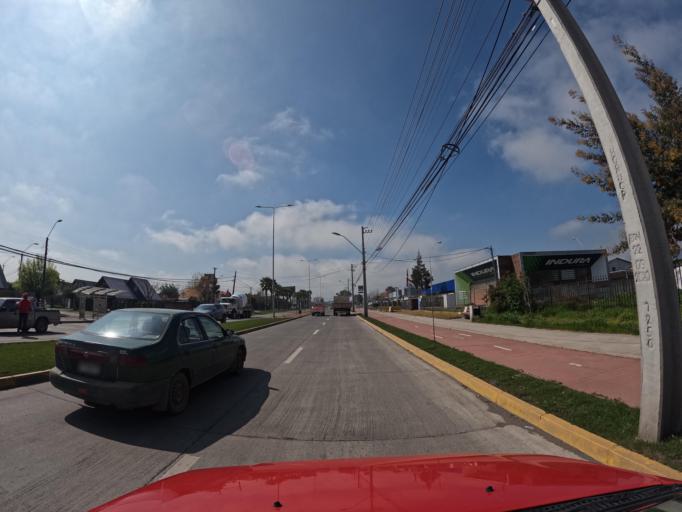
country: CL
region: Maule
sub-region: Provincia de Curico
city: Curico
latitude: -34.9767
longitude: -71.2131
